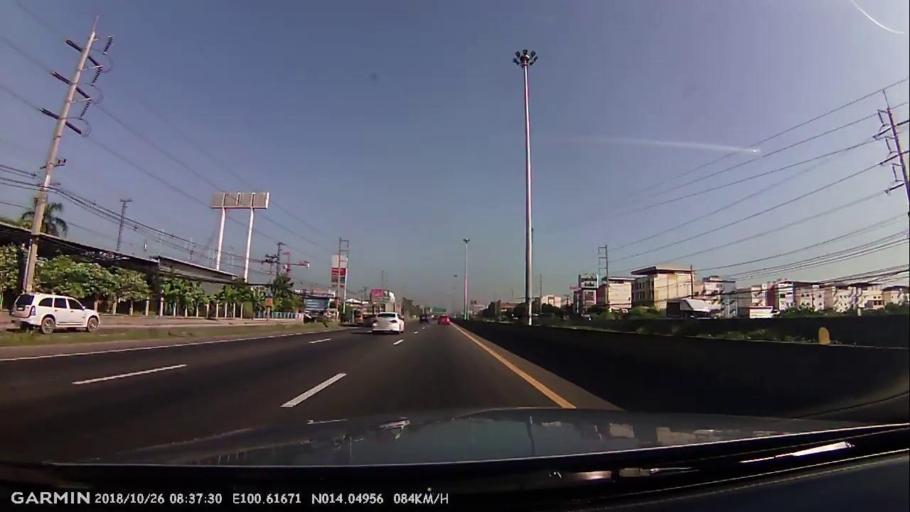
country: TH
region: Pathum Thani
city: Khlong Luang
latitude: 14.0497
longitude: 100.6165
